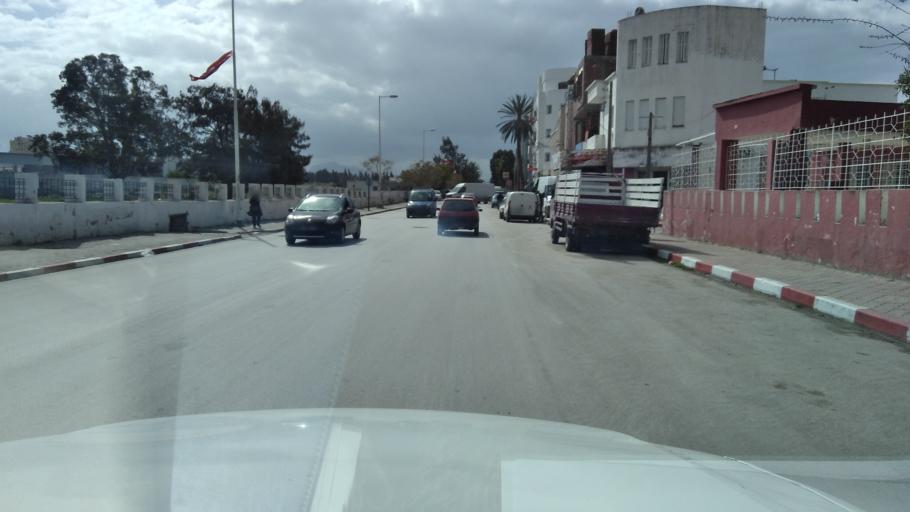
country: TN
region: Bin 'Arus
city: Ben Arous
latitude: 36.7509
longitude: 10.2243
